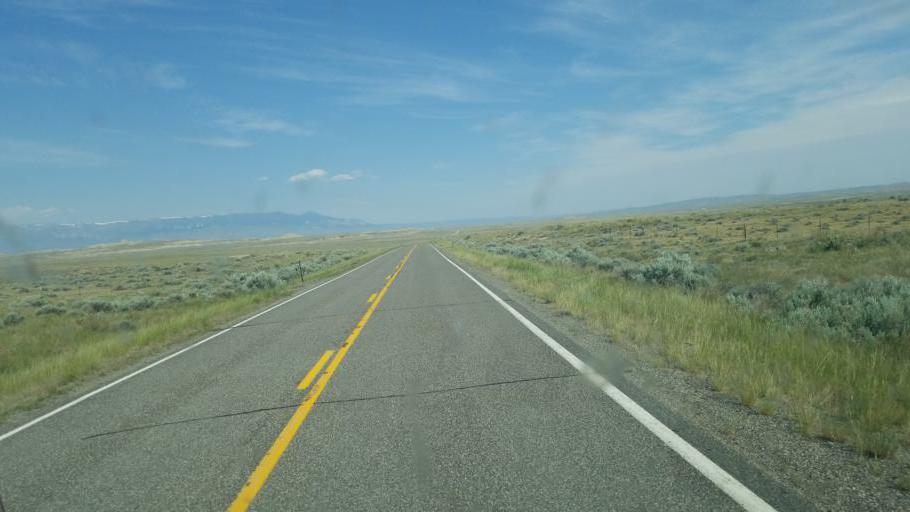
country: US
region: Wyoming
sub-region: Park County
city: Powell
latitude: 44.8012
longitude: -108.9614
